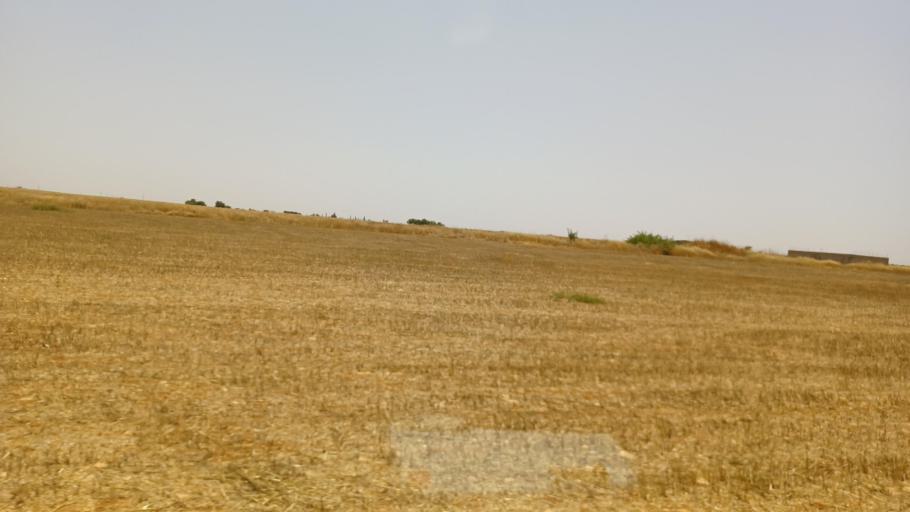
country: CY
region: Ammochostos
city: Avgorou
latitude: 35.0558
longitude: 33.8413
